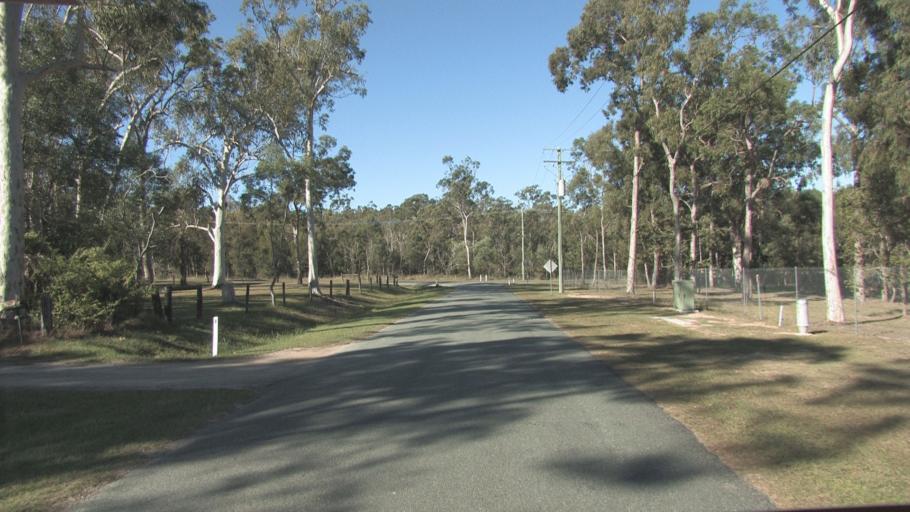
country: AU
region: Queensland
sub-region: Logan
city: Chambers Flat
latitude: -27.7349
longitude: 153.0703
